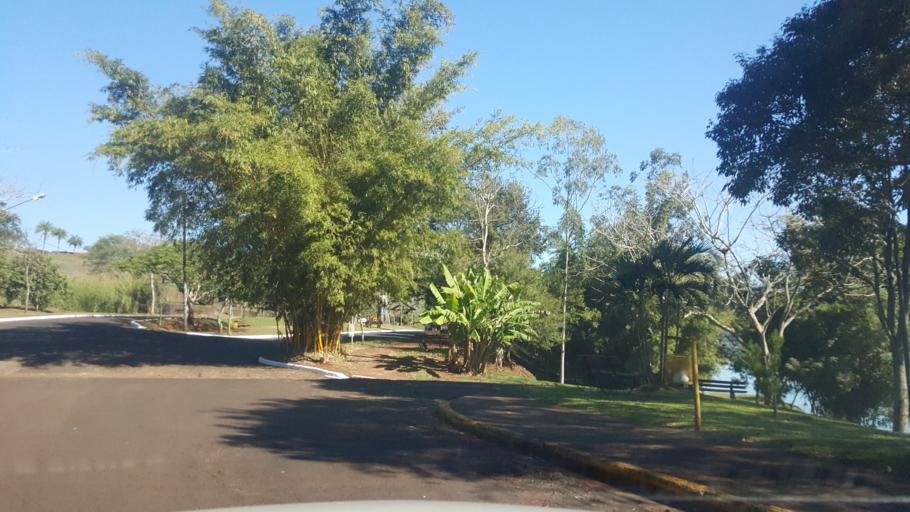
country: AR
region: Misiones
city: Puerto Rico
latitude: -26.7920
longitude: -55.0263
